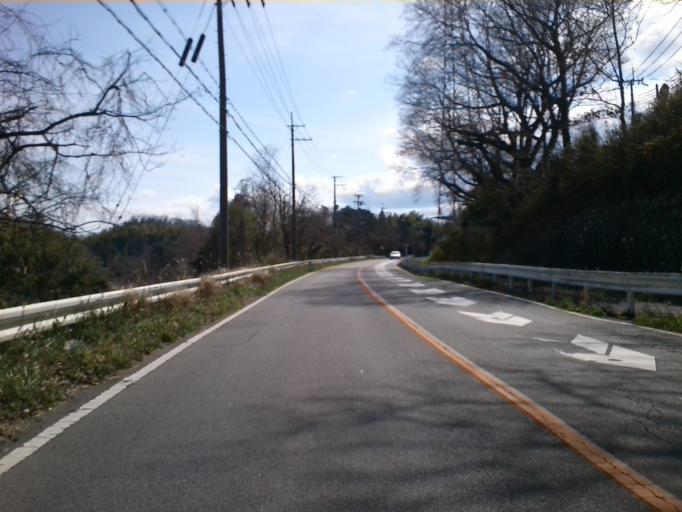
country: JP
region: Nara
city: Nara-shi
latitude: 34.7280
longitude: 135.8580
